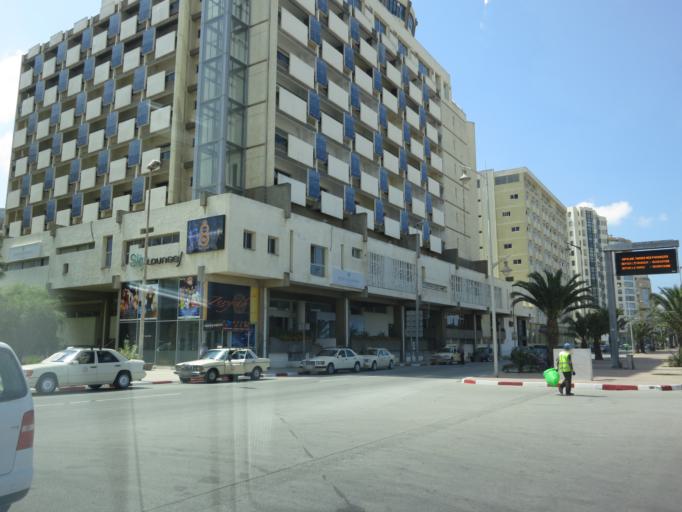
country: MA
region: Tanger-Tetouan
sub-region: Tanger-Assilah
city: Tangier
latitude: 35.7777
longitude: -5.7994
